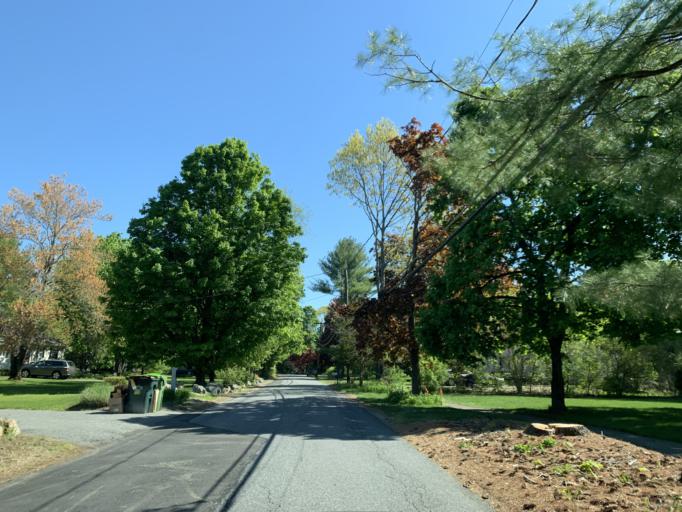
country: US
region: Massachusetts
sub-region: Middlesex County
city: Sudbury
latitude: 42.4159
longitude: -71.4109
